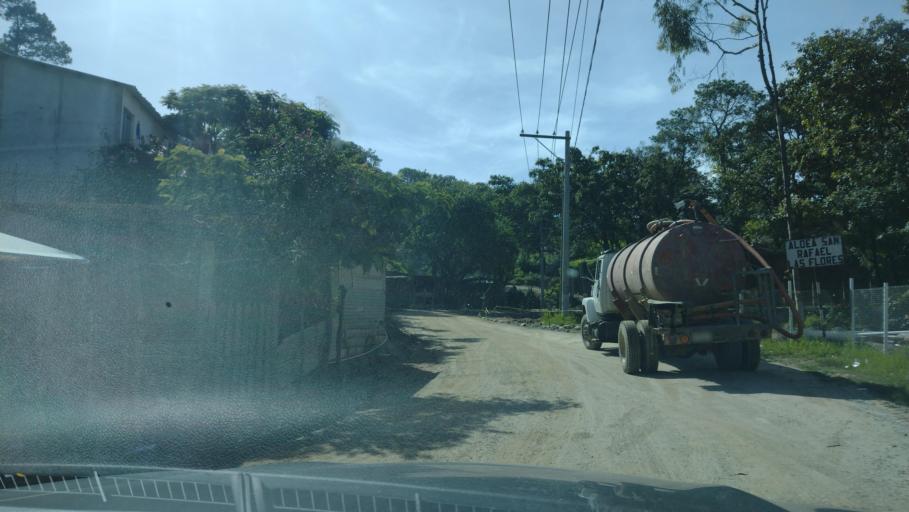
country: GT
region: Guatemala
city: Chinautla
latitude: 14.7627
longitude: -90.5255
